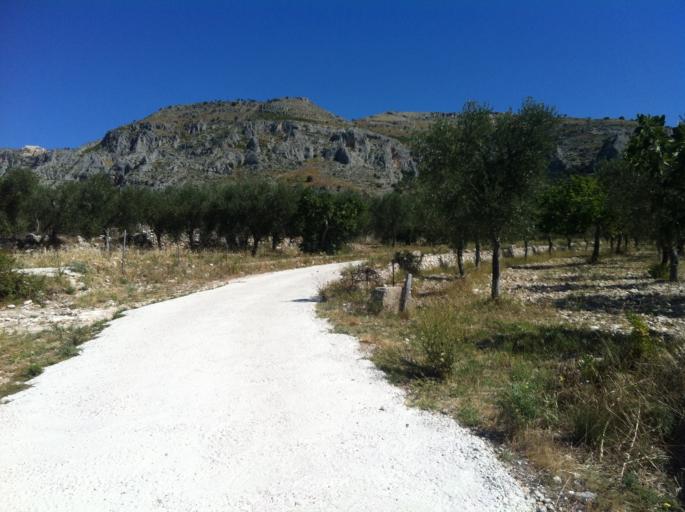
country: IT
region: Apulia
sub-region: Provincia di Foggia
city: Manfredonia
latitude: 41.6592
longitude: 15.9136
